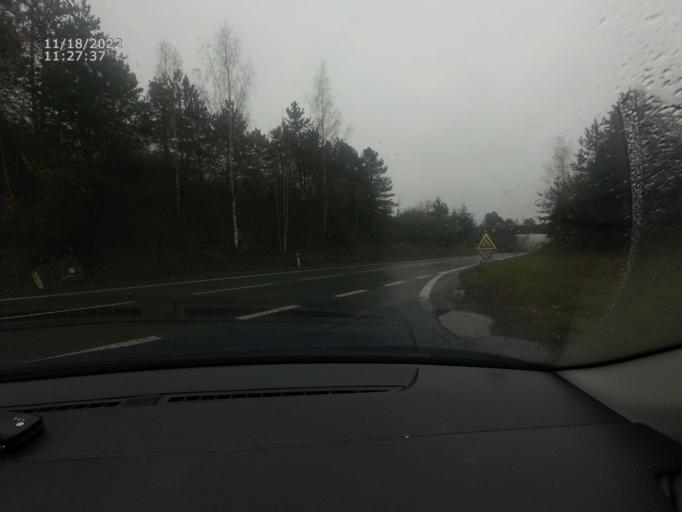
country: CZ
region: Plzensky
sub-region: Okres Rokycany
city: Rokycany
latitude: 49.7534
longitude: 13.5767
